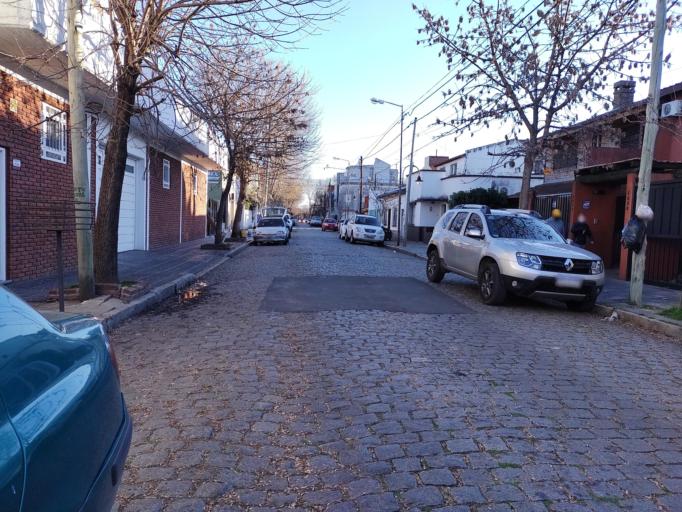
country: AR
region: Buenos Aires
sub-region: Partido de Tigre
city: Tigre
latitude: -34.4494
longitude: -58.5464
